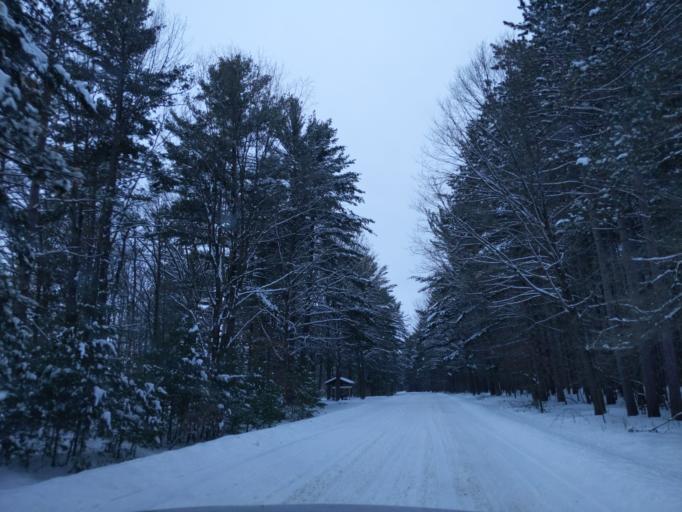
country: US
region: Wisconsin
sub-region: Marathon County
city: Marathon
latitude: 44.7657
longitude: -89.8695
